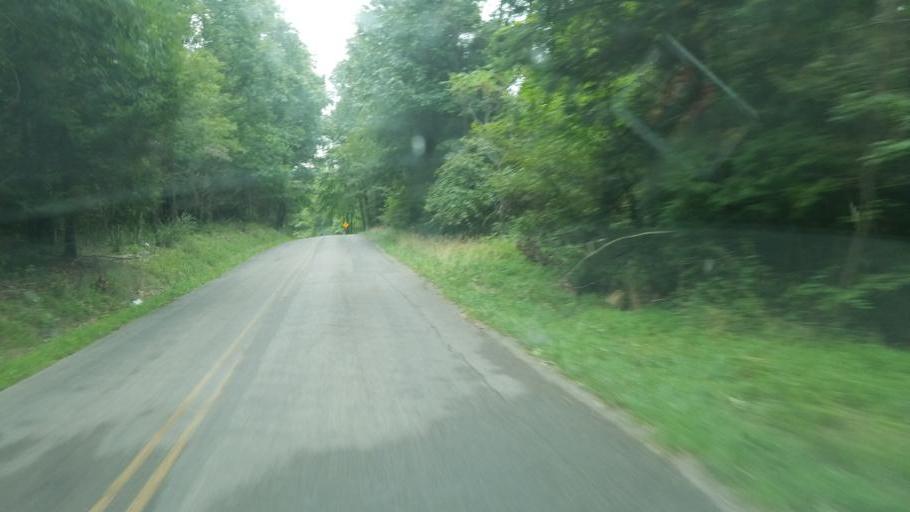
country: US
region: Pennsylvania
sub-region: Clarion County
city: Marianne
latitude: 41.1767
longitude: -79.4677
